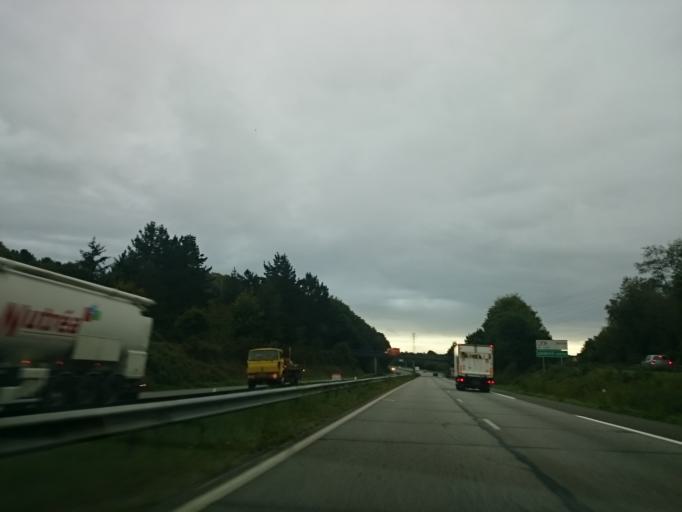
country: FR
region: Brittany
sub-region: Departement du Finistere
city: Quimper
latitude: 48.0214
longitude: -4.0833
